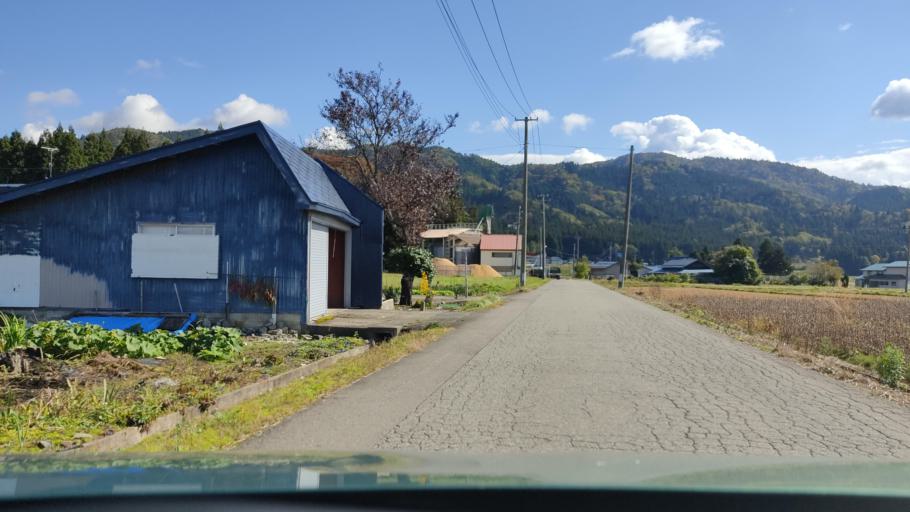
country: JP
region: Akita
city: Yokotemachi
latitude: 39.4036
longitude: 140.5824
